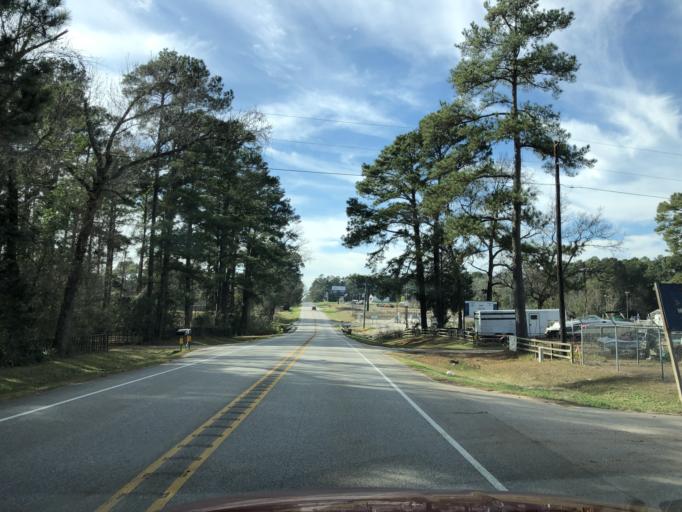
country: US
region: Texas
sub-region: Montgomery County
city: Panorama Village
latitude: 30.4371
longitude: -95.6223
